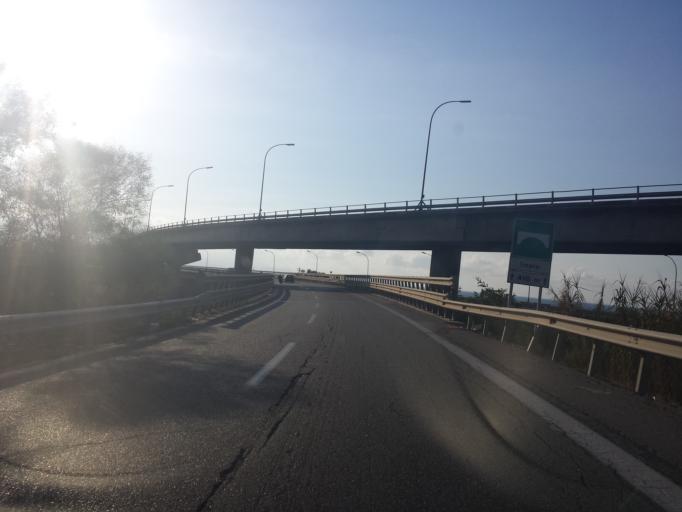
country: IT
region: Sicily
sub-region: Palermo
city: Campofelice di Roccella
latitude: 37.9790
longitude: 13.8272
